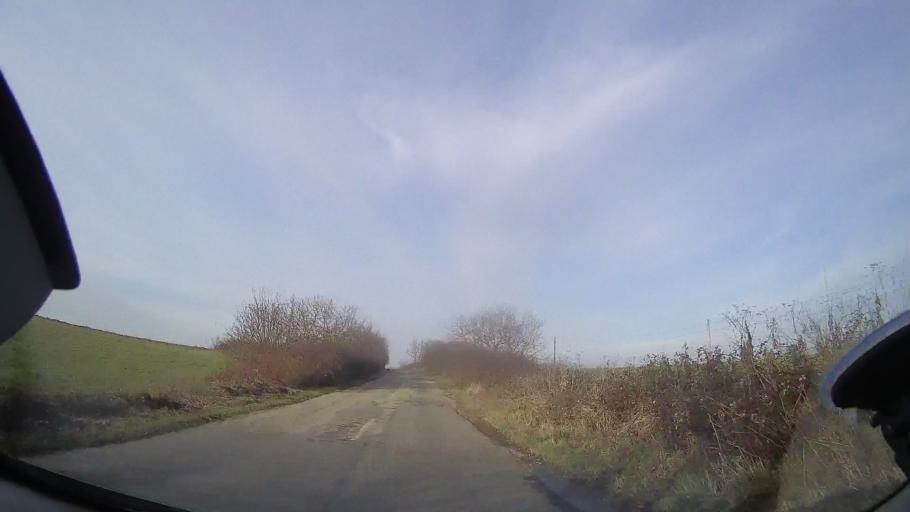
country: RO
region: Bihor
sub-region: Comuna Spinus
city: Spinus
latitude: 47.2119
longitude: 22.1783
